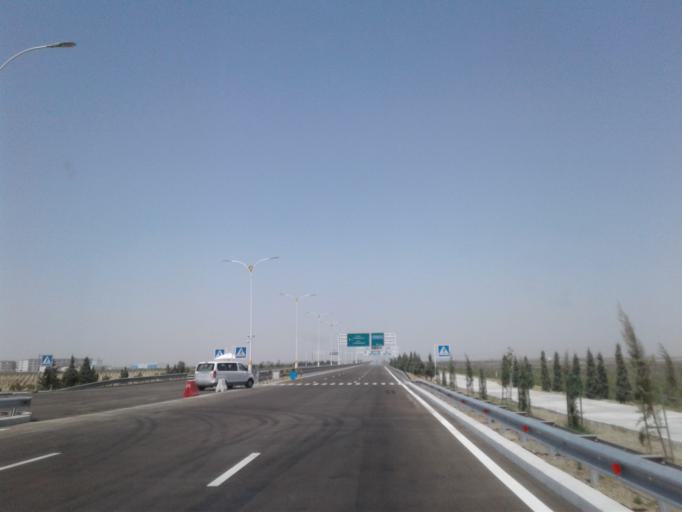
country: TM
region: Balkan
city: Turkmenbasy
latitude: 39.9721
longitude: 52.8675
